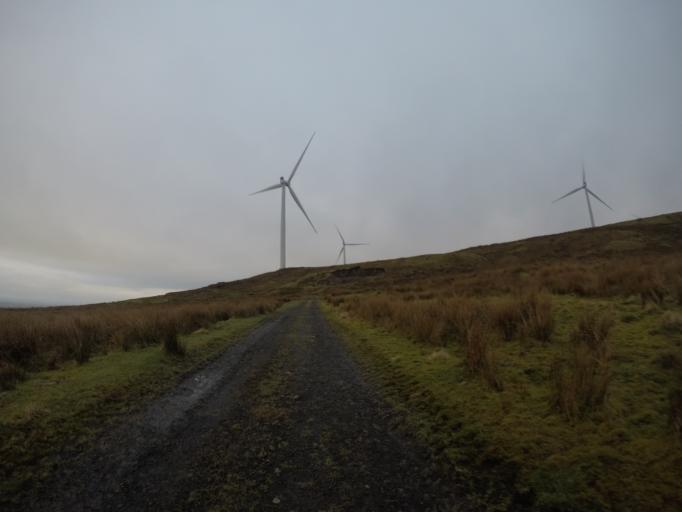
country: GB
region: Scotland
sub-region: North Ayrshire
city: Dalry
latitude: 55.7382
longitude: -4.7703
